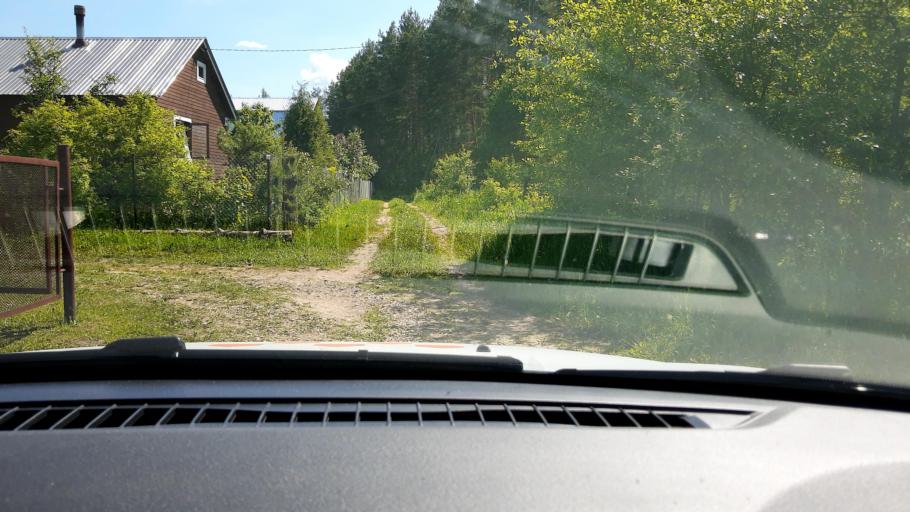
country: RU
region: Nizjnij Novgorod
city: Surovatikha
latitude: 55.8663
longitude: 43.9643
